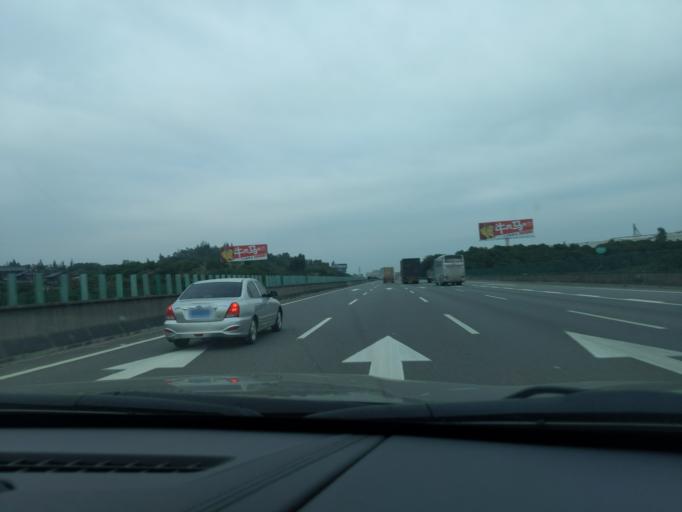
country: CN
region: Fujian
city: Anhai
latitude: 24.7168
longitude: 118.4002
